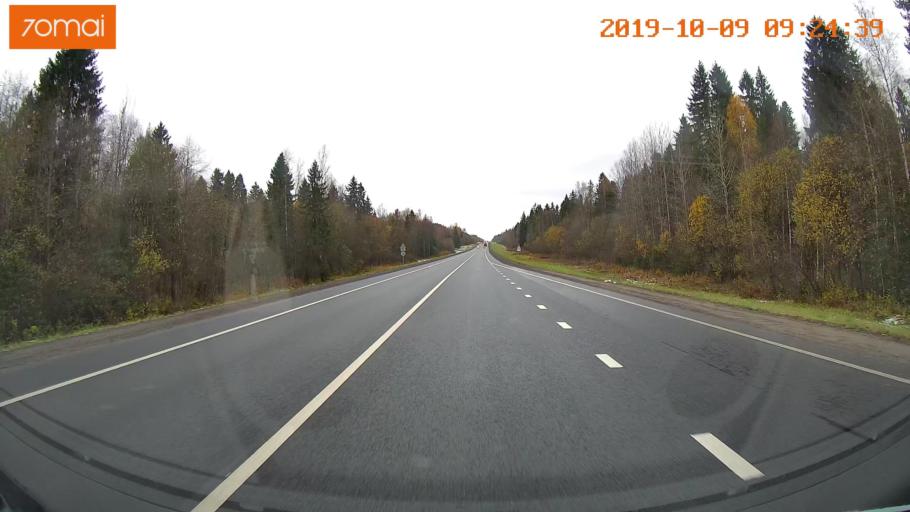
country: RU
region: Vologda
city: Vologda
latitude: 59.0814
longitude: 40.0130
